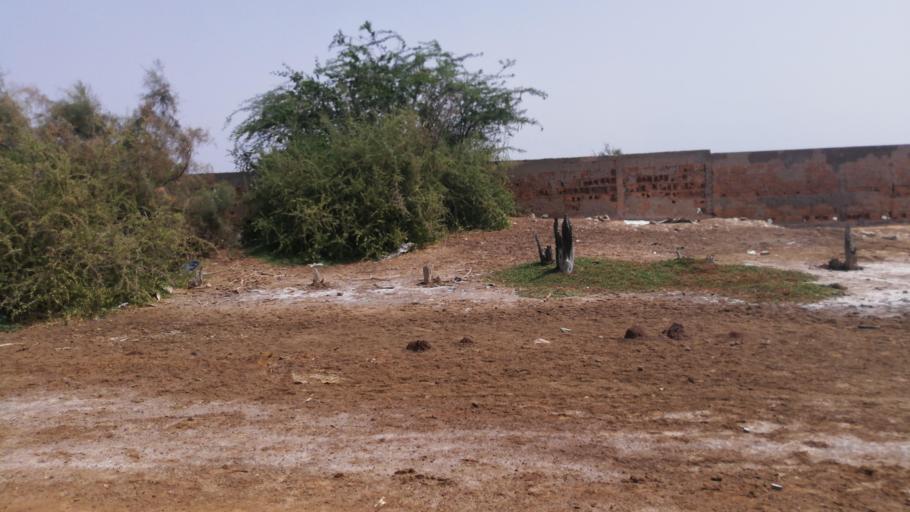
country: SN
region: Saint-Louis
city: Saint-Louis
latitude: 16.3589
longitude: -16.2743
